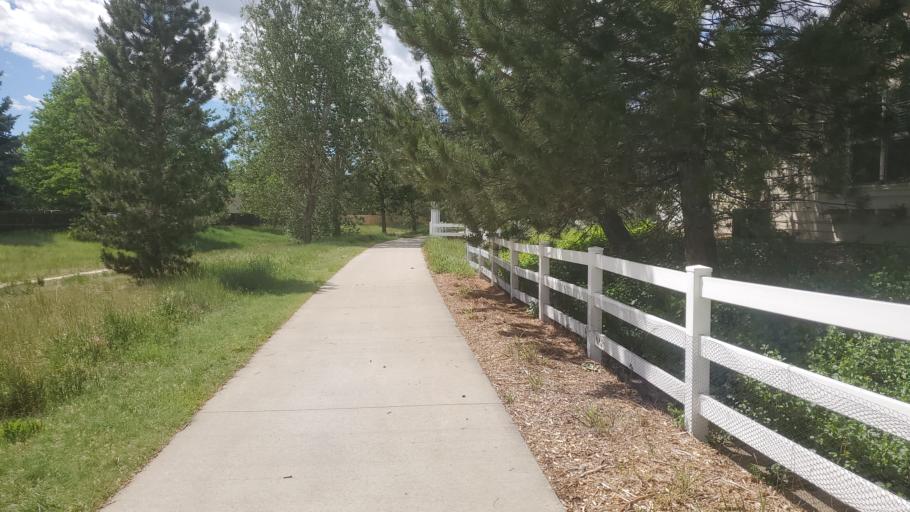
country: US
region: Colorado
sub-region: Adams County
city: Aurora
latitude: 39.6696
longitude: -104.8405
